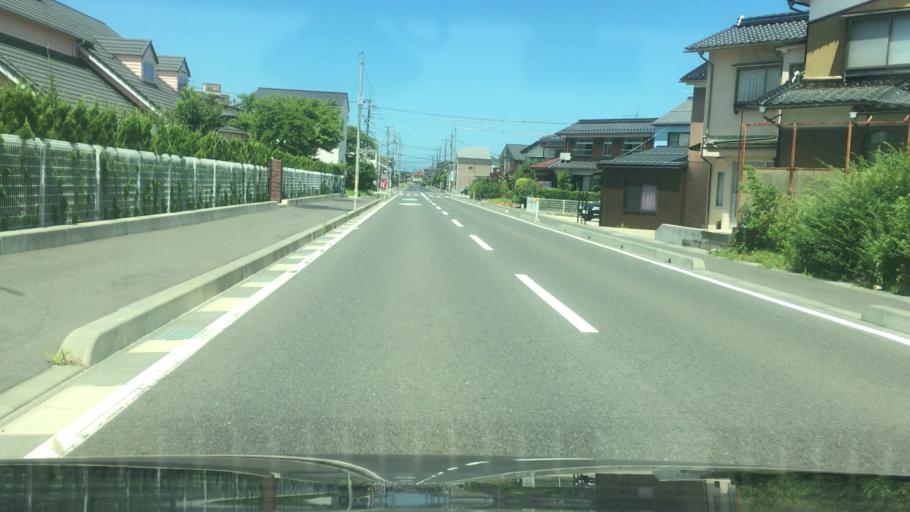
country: JP
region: Tottori
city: Tottori
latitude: 35.4819
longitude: 134.2309
